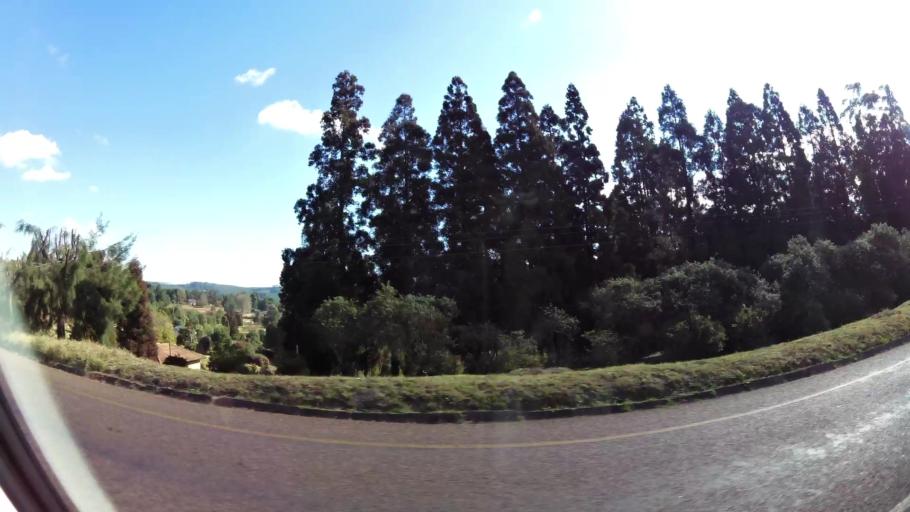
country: ZA
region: Limpopo
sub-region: Capricorn District Municipality
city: Mankoeng
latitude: -23.8996
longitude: 29.9935
